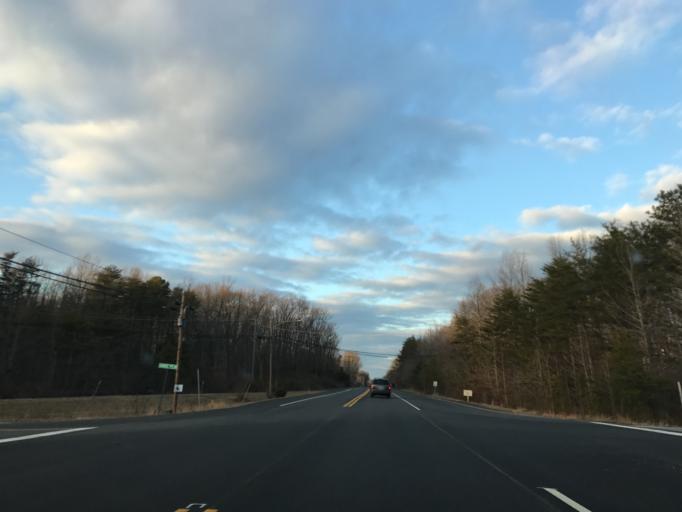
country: US
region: Maryland
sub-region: Cecil County
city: North East
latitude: 39.5786
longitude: -75.9435
